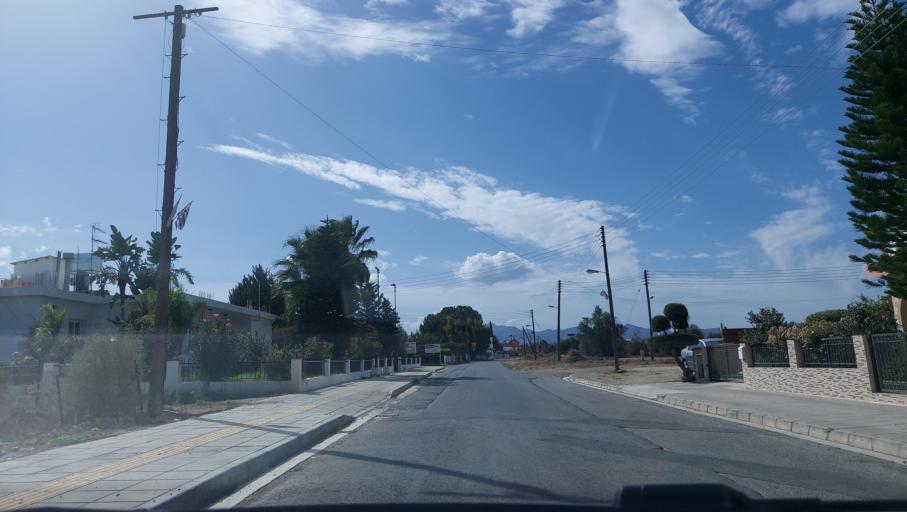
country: CY
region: Lefkosia
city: Pano Deftera
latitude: 35.0711
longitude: 33.2614
